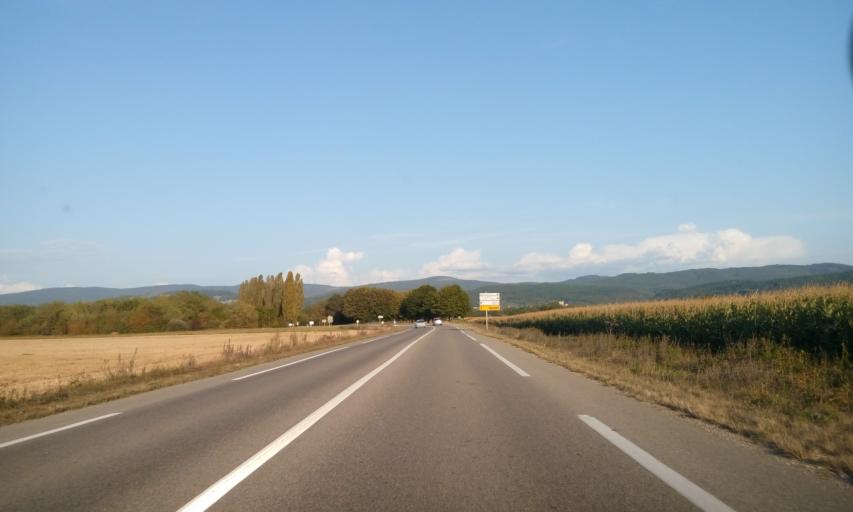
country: FR
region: Rhone-Alpes
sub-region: Departement de l'Ain
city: Ambronay
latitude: 46.0387
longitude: 5.3486
